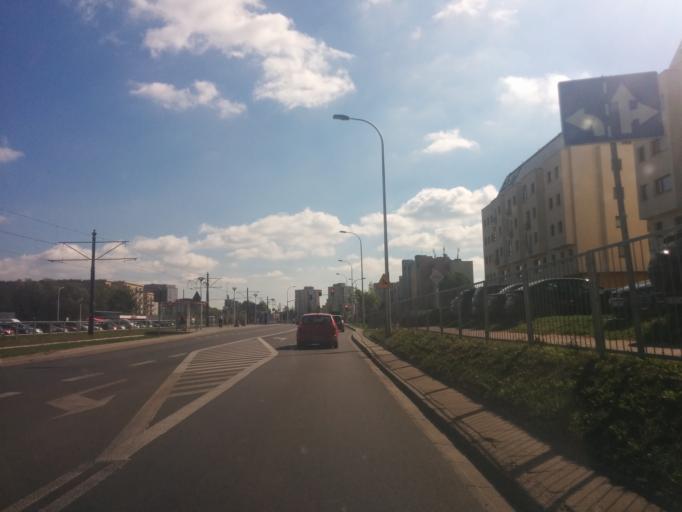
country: PL
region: Masovian Voivodeship
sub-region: Warszawa
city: Bialoleka
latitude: 52.3193
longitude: 20.9506
